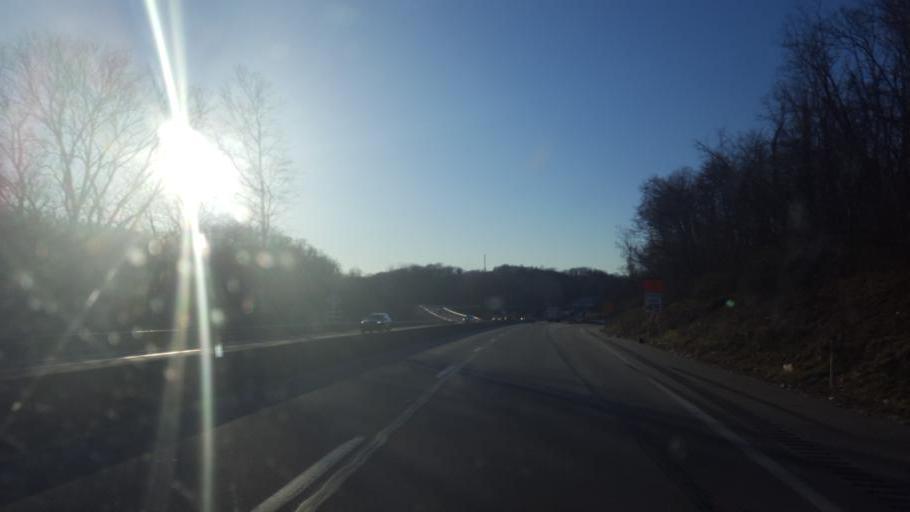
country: US
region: Pennsylvania
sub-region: Washington County
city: Charleroi
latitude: 40.1132
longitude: -79.9375
